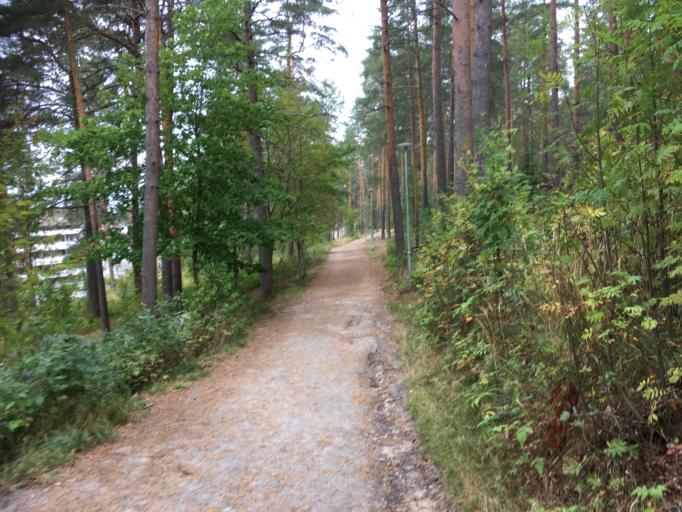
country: FI
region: Central Finland
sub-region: Jyvaeskylae
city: Jyvaeskylae
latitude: 62.2412
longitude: 25.7360
